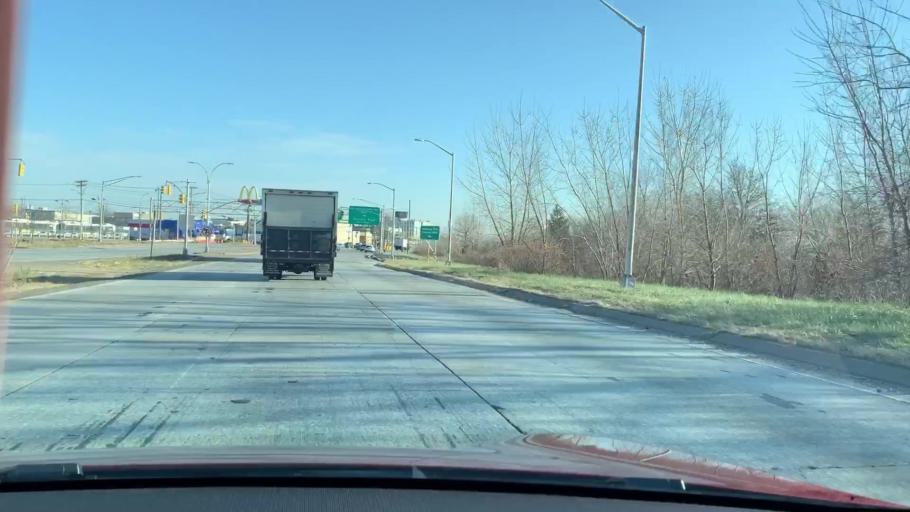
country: US
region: New York
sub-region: Queens County
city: Jamaica
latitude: 40.6605
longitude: -73.7763
